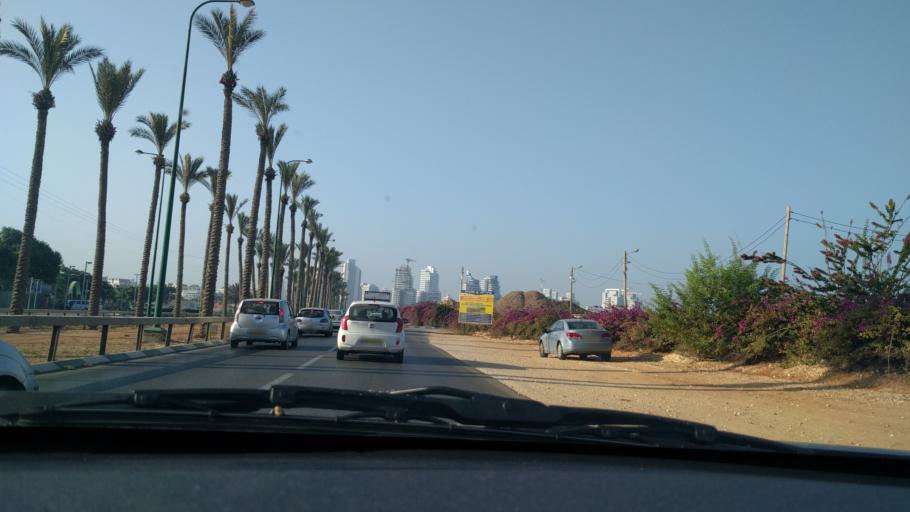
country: IL
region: Central District
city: Netanya
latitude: 32.2917
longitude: 34.8423
